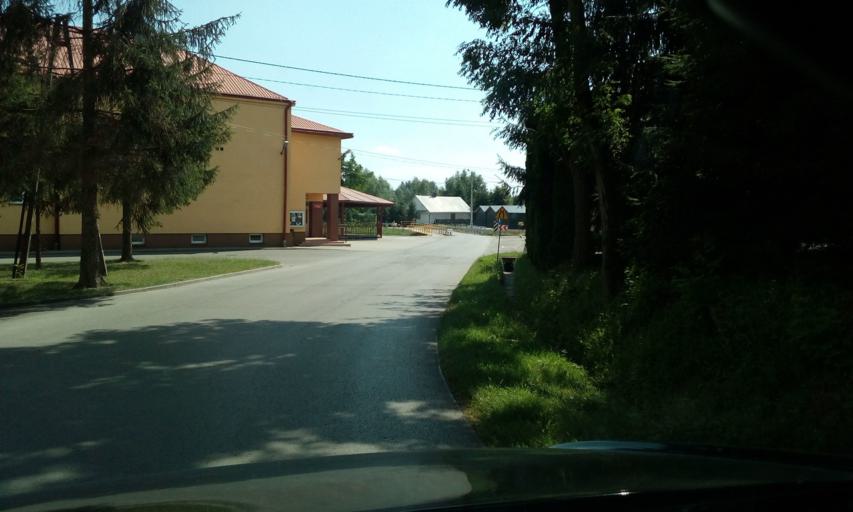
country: PL
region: Subcarpathian Voivodeship
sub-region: Powiat lancucki
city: Wysoka
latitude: 50.0447
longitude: 22.2496
